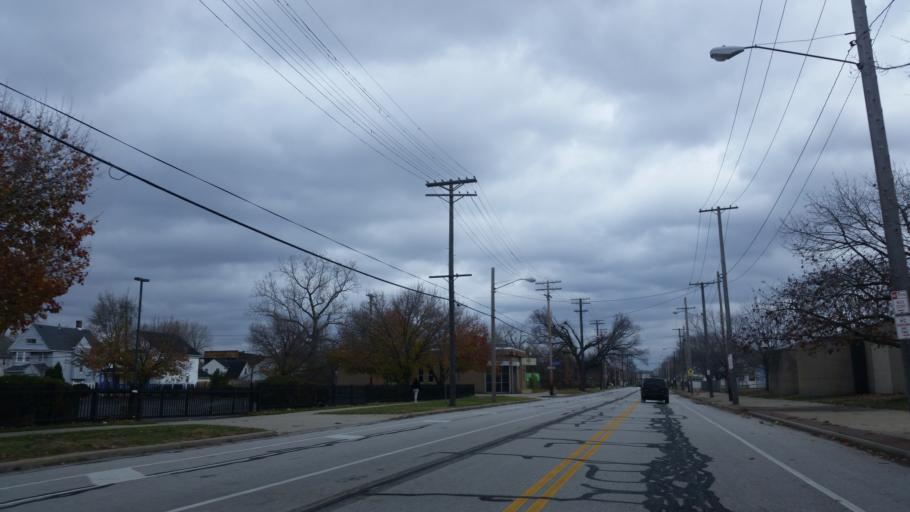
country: US
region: Ohio
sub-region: Cuyahoga County
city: Newburgh Heights
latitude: 41.4934
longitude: -81.6503
